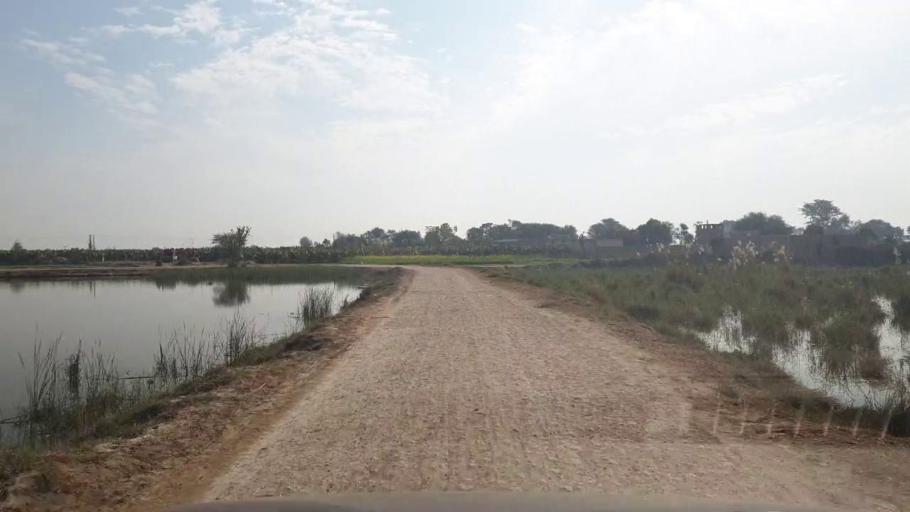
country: PK
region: Sindh
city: Hala
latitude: 25.9956
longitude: 68.4404
